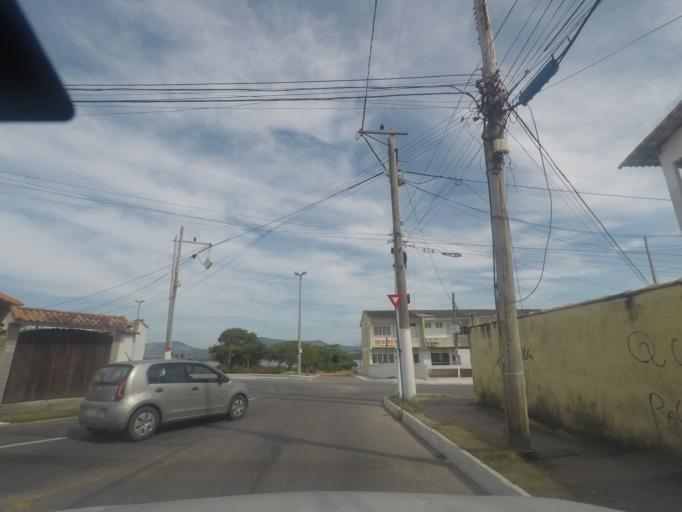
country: BR
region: Rio de Janeiro
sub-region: Marica
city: Marica
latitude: -22.9571
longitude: -42.8146
